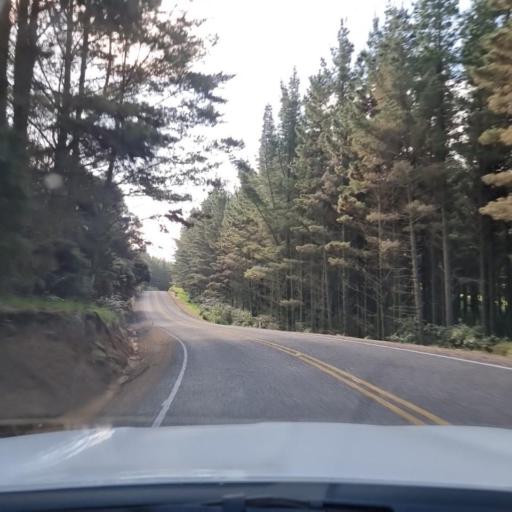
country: NZ
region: Northland
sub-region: Kaipara District
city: Dargaville
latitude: -36.2742
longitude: 174.0554
